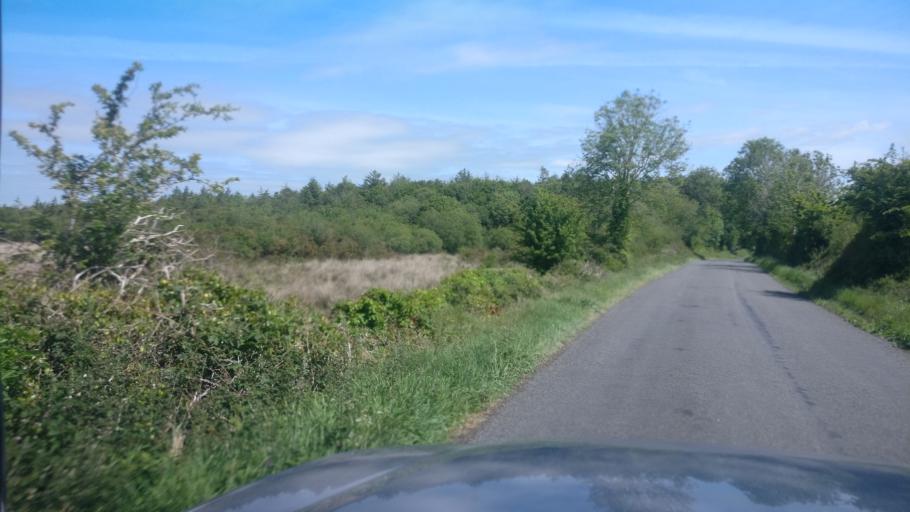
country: IE
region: Connaught
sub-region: County Galway
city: Gort
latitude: 53.1256
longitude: -8.7811
